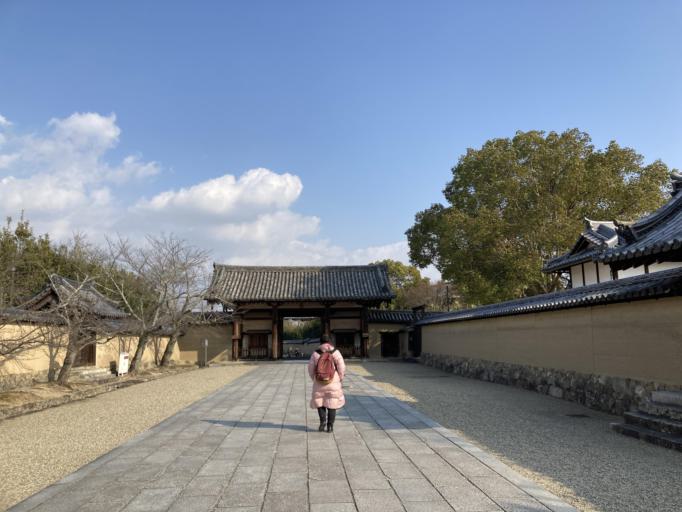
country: JP
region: Nara
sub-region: Ikoma-shi
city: Ikoma
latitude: 34.6138
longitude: 135.7362
